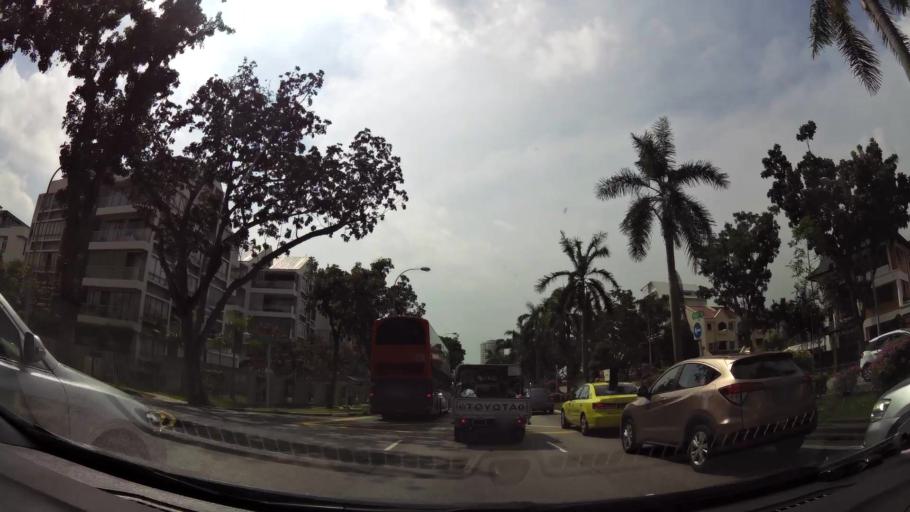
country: SG
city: Singapore
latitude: 1.3102
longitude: 103.9080
